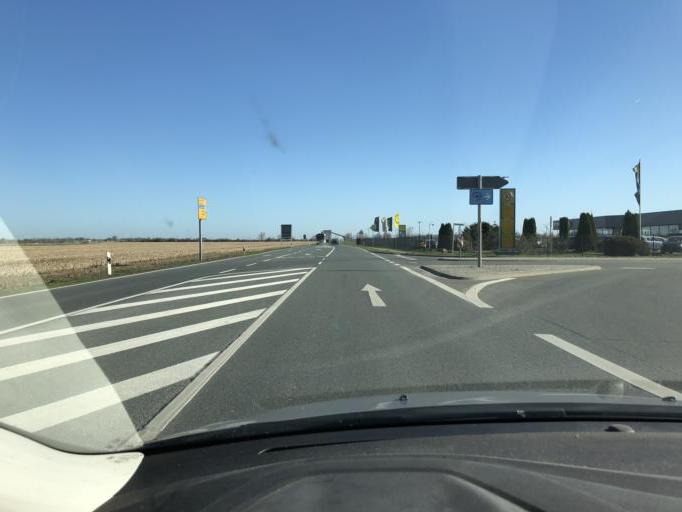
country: DE
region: Saxony-Anhalt
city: Stassfurt
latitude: 51.8670
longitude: 11.6021
